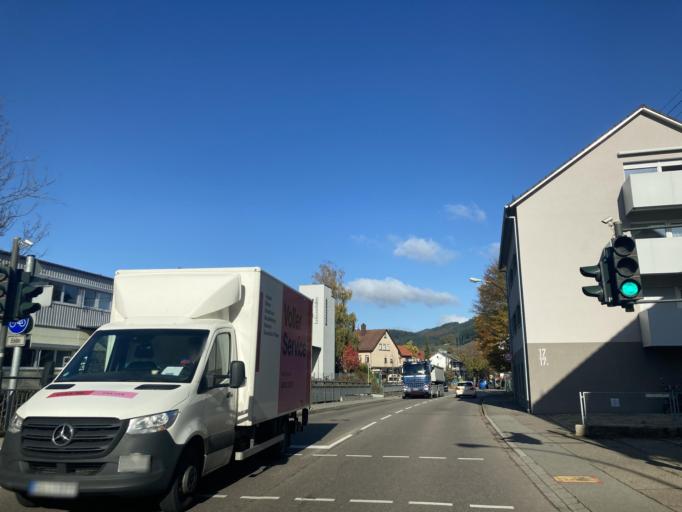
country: DE
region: Baden-Wuerttemberg
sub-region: Freiburg Region
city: Hofstetten
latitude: 48.2736
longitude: 8.0906
